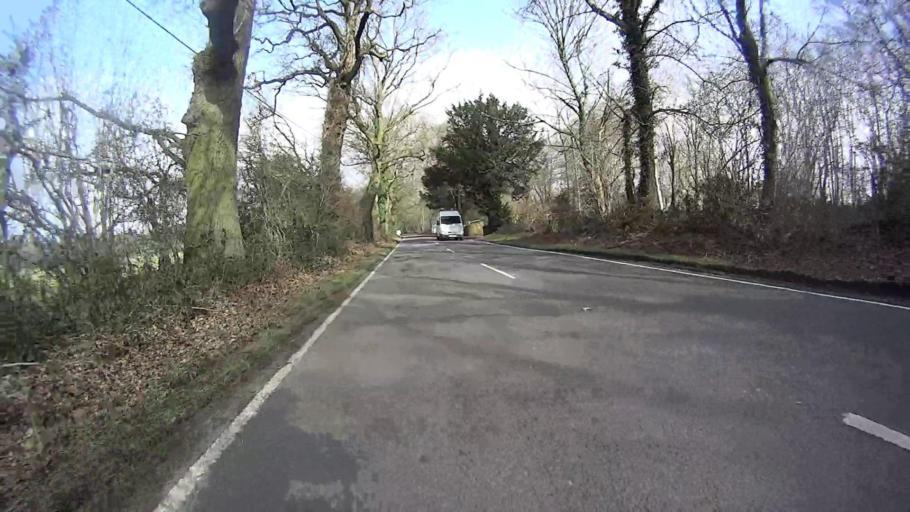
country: GB
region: England
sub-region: Surrey
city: Headley
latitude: 51.2564
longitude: -0.2729
